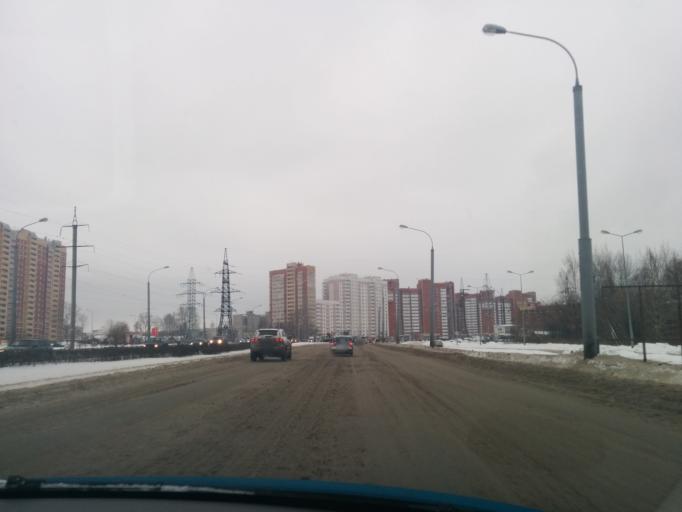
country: RU
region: Perm
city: Perm
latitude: 57.9897
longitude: 56.2960
